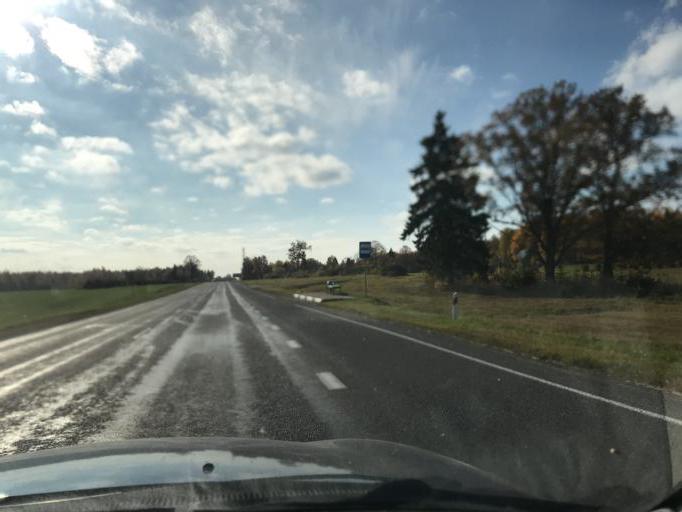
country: BY
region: Grodnenskaya
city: Voranava
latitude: 54.1801
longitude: 25.3351
